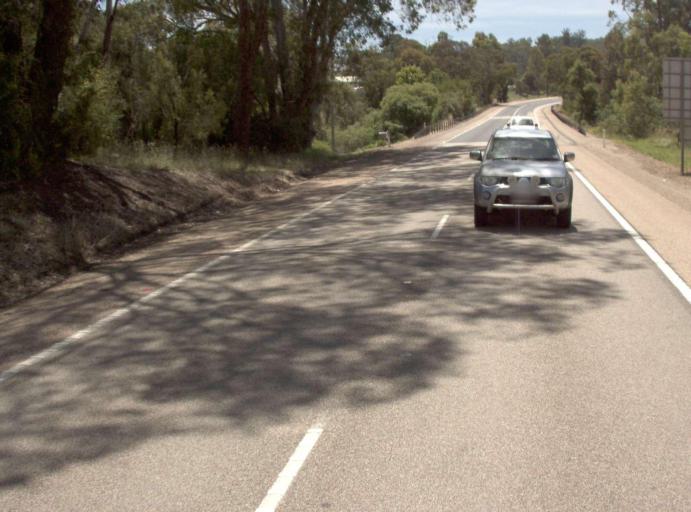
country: AU
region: Victoria
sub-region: East Gippsland
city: Bairnsdale
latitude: -37.7166
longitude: 147.8054
